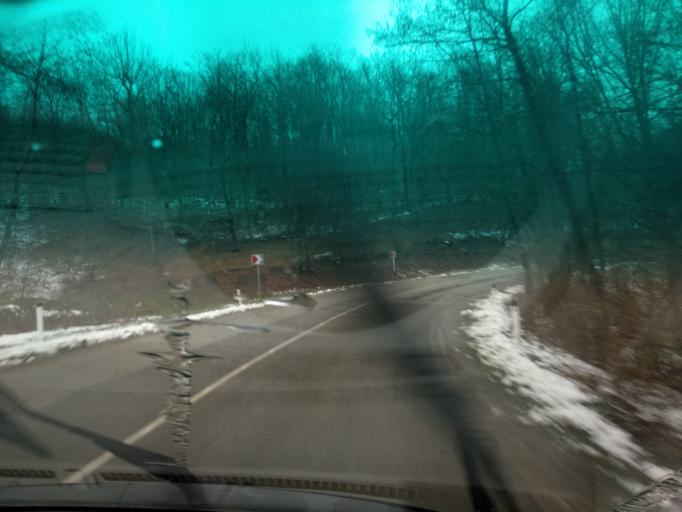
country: RU
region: Krasnodarskiy
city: Khadyzhensk
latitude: 44.2281
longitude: 39.3836
